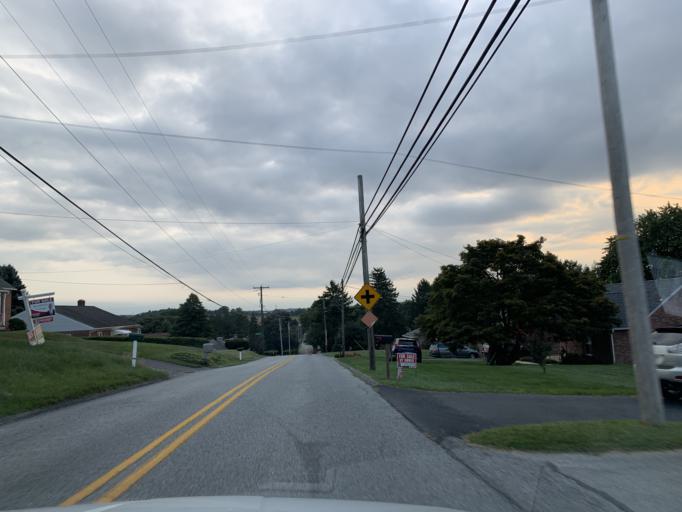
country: US
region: Pennsylvania
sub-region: York County
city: Emigsville
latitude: 40.0008
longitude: -76.7305
